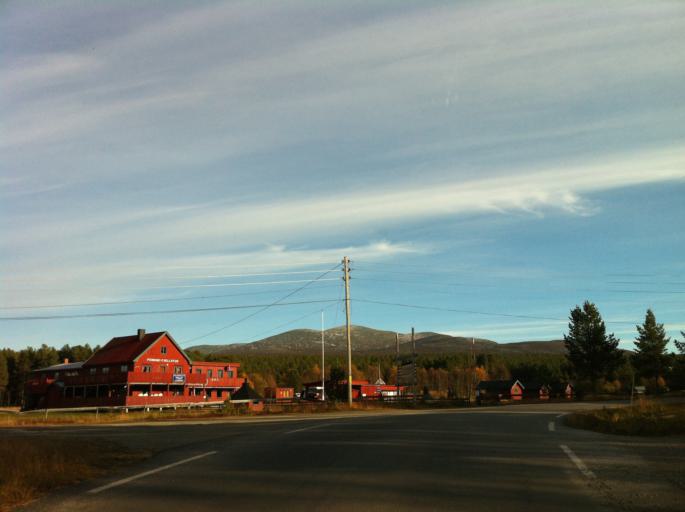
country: NO
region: Hedmark
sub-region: Engerdal
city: Engerdal
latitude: 62.1672
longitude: 11.9417
